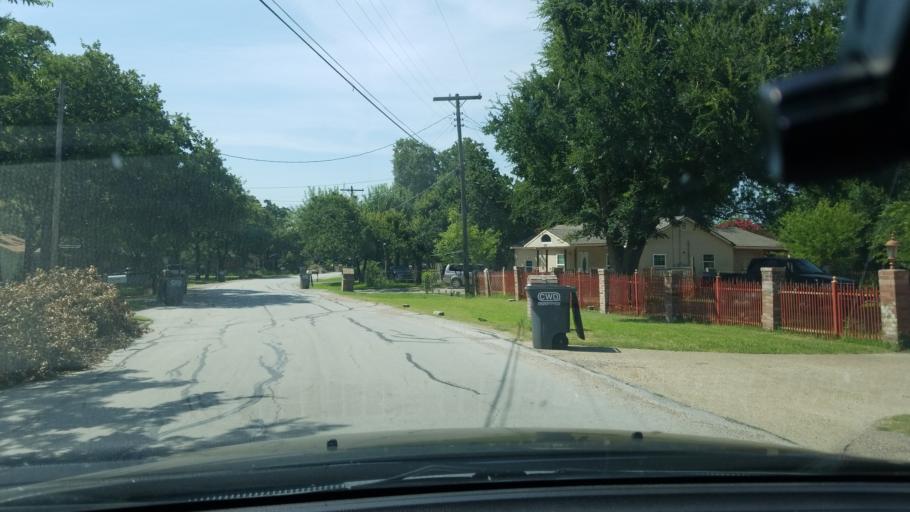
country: US
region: Texas
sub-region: Dallas County
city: Balch Springs
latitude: 32.7315
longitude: -96.6338
